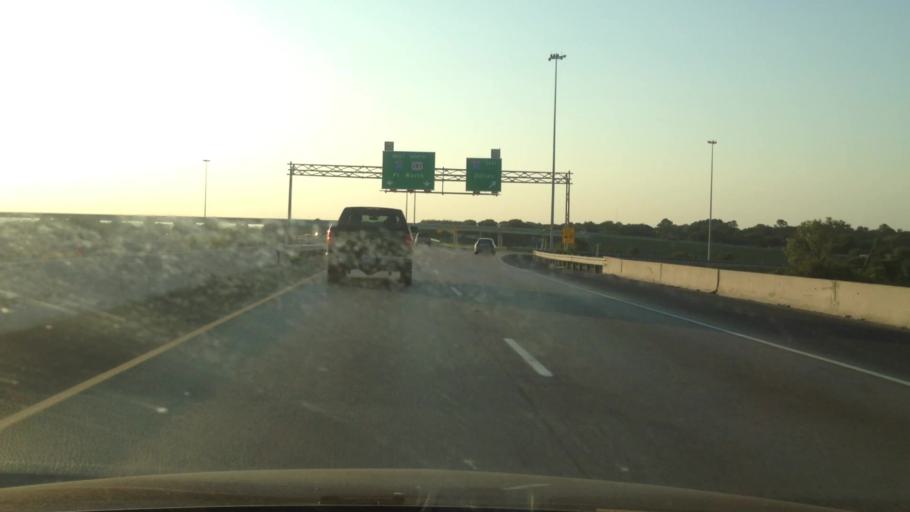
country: US
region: Texas
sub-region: Tarrant County
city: Kennedale
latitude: 32.6679
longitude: -97.2035
